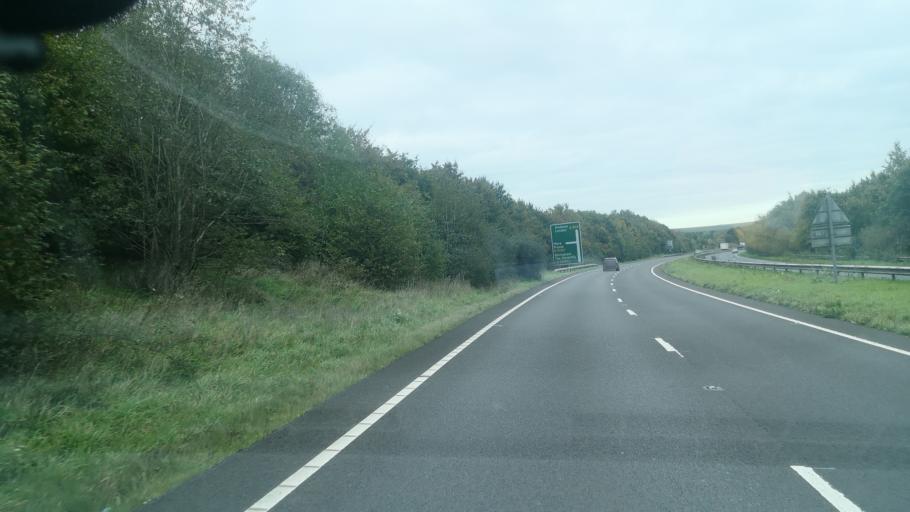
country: GB
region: England
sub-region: Wiltshire
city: Mere
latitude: 51.0864
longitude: -2.3050
